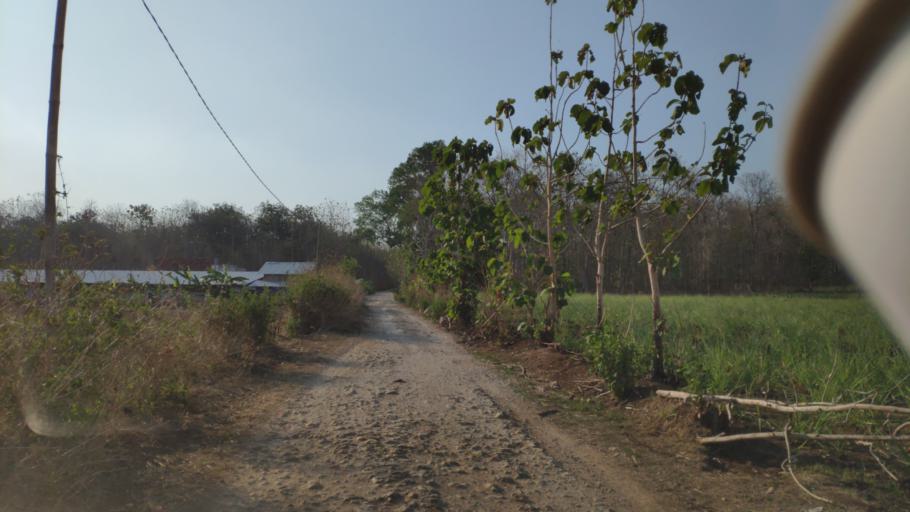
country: ID
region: Central Java
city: Pelem
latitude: -6.9948
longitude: 111.1880
